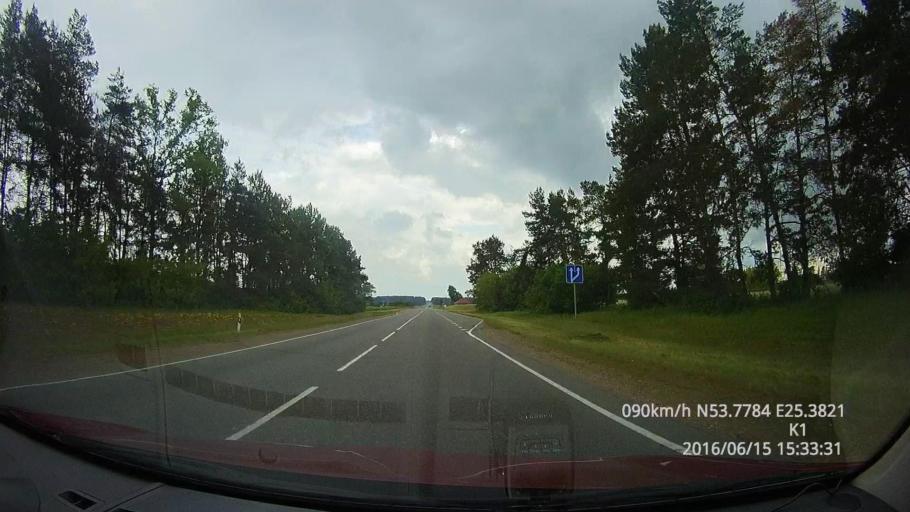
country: BY
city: Berezovka
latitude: 53.7777
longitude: 25.3824
